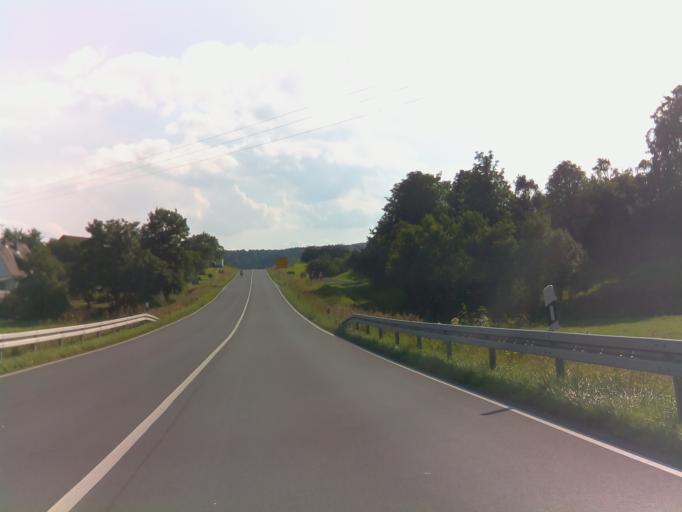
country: DE
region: Bavaria
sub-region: Regierungsbezirk Unterfranken
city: Hammelburg
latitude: 50.1065
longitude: 9.8487
